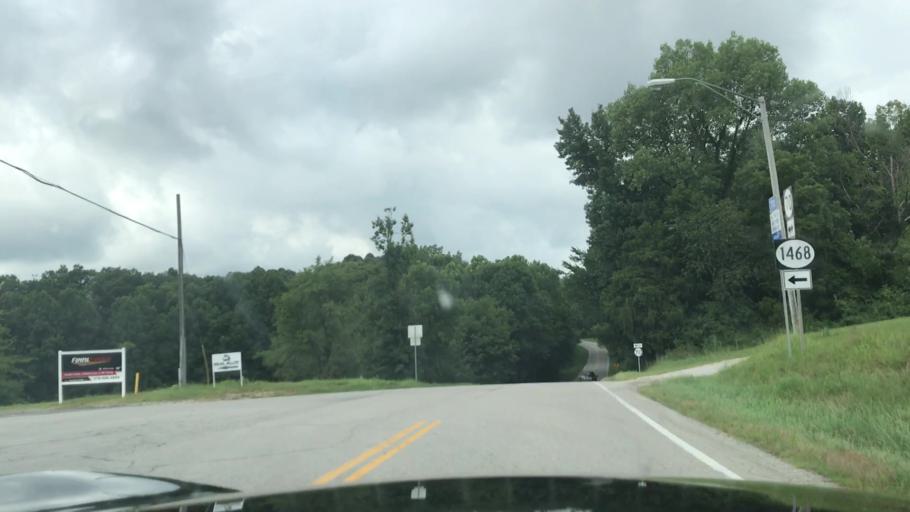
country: US
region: Kentucky
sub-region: Butler County
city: Morgantown
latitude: 37.2106
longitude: -86.7183
